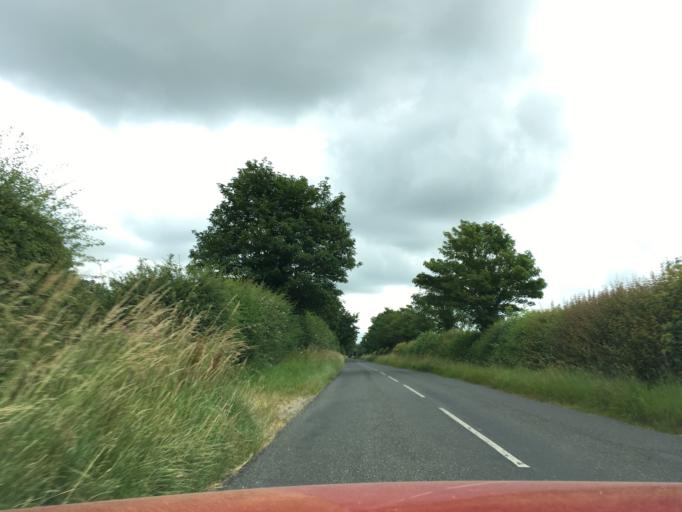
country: GB
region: England
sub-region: Oxfordshire
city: Shipton under Wychwood
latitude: 51.9094
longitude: -1.5953
